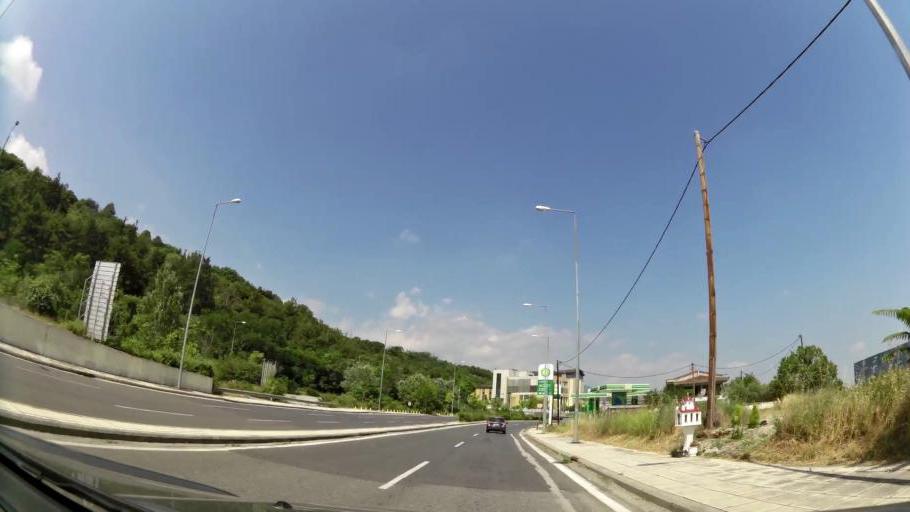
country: GR
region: Central Macedonia
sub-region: Nomos Imathias
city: Veroia
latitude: 40.5067
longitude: 22.2270
